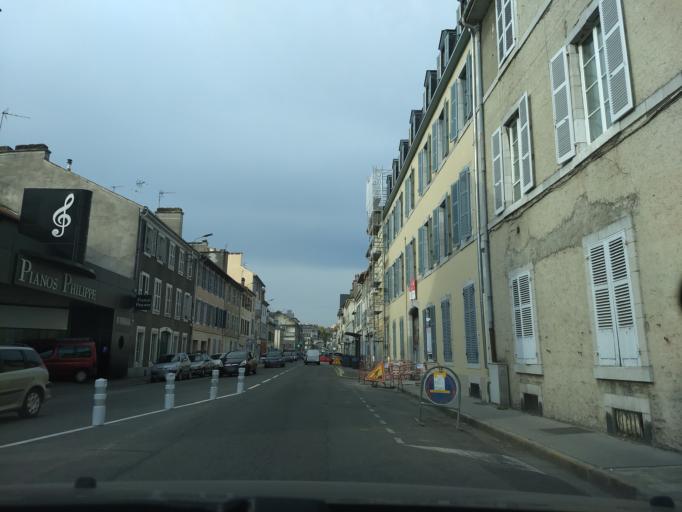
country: FR
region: Aquitaine
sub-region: Departement des Pyrenees-Atlantiques
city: Jurancon
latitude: 43.2903
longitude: -0.3791
